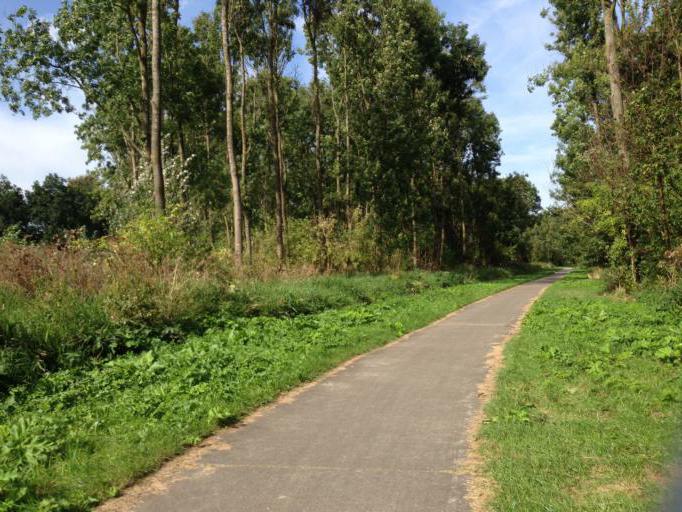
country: NL
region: North Holland
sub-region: Gemeente Huizen
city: Huizen
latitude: 52.3505
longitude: 5.2764
